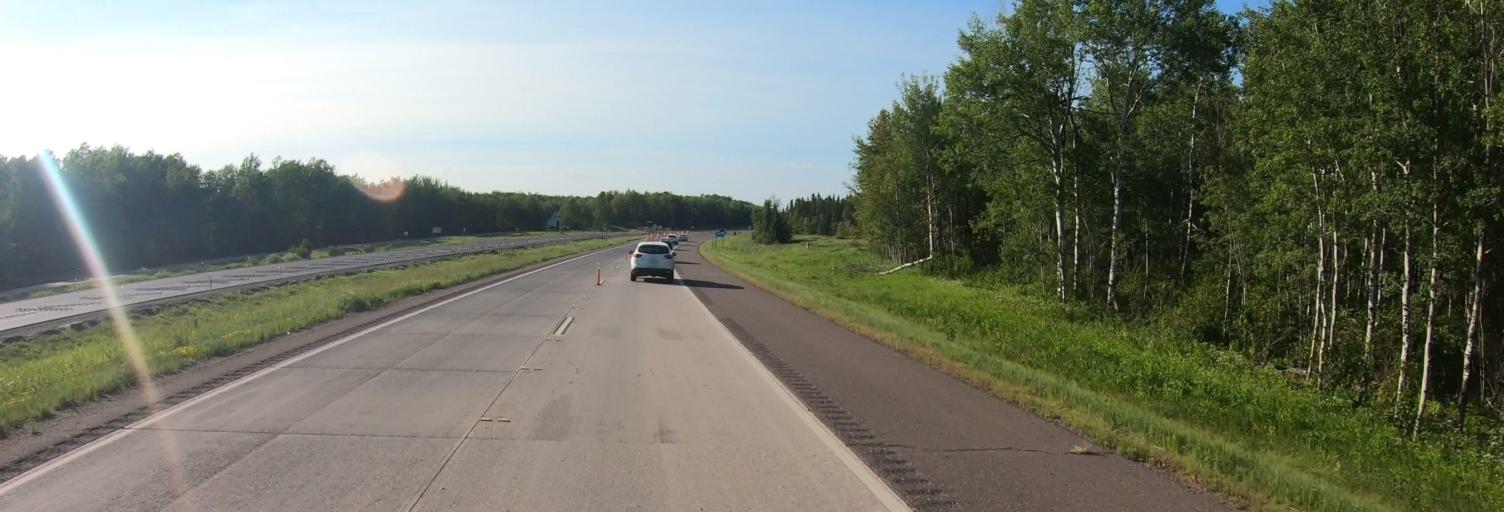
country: US
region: Minnesota
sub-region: Saint Louis County
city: Hermantown
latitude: 46.8813
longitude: -92.3503
